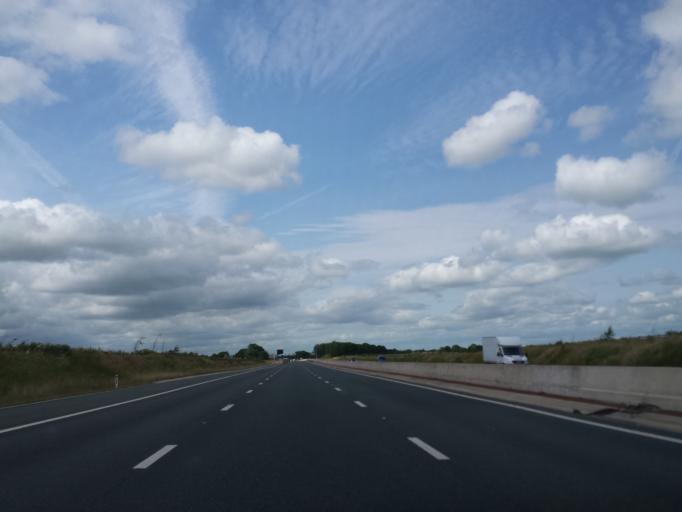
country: GB
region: England
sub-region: North Yorkshire
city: Bedale
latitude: 54.2861
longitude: -1.5443
